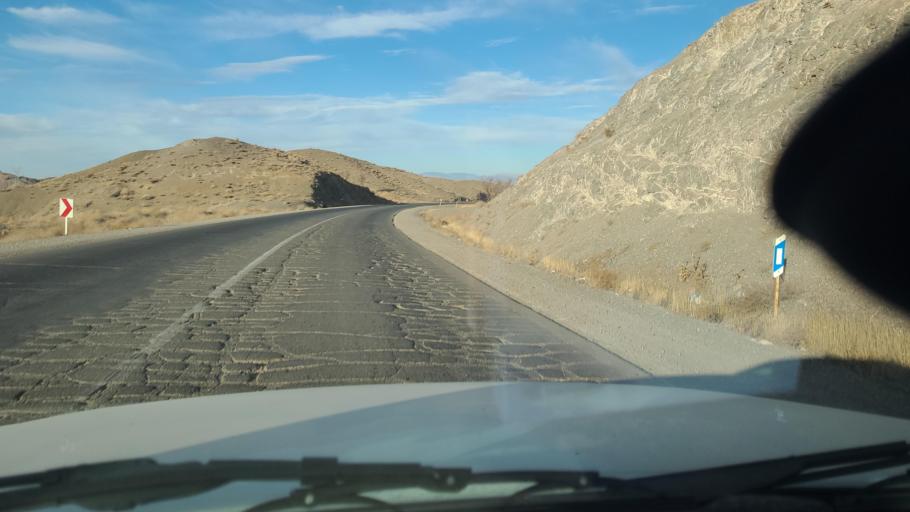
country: IR
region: Razavi Khorasan
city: Sabzevar
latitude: 36.4138
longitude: 57.5512
